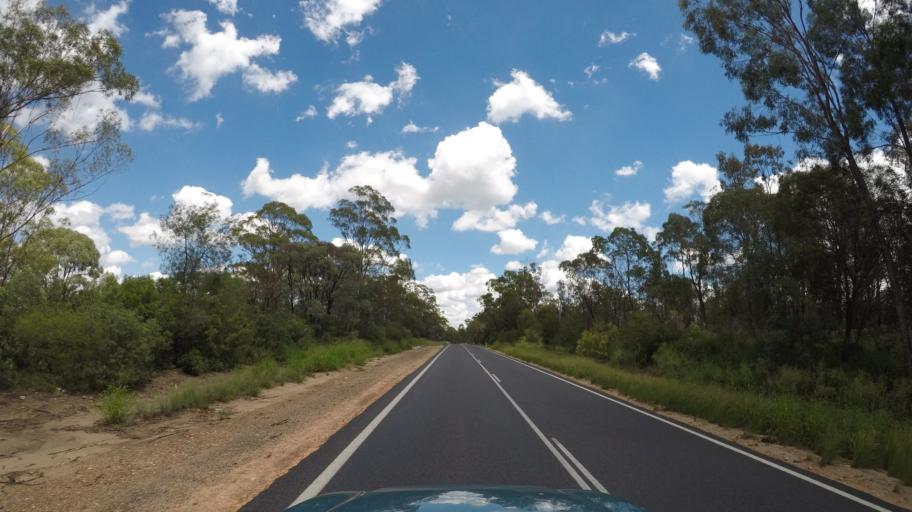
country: AU
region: Queensland
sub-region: Goondiwindi
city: Goondiwindi
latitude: -28.0027
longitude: 150.9080
